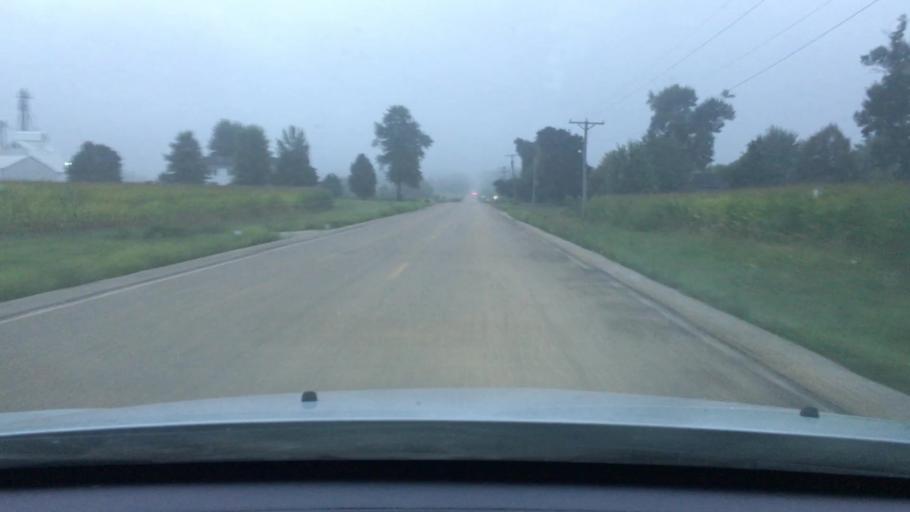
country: US
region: Illinois
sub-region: DeKalb County
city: Waterman
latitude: 41.7820
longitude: -88.7739
